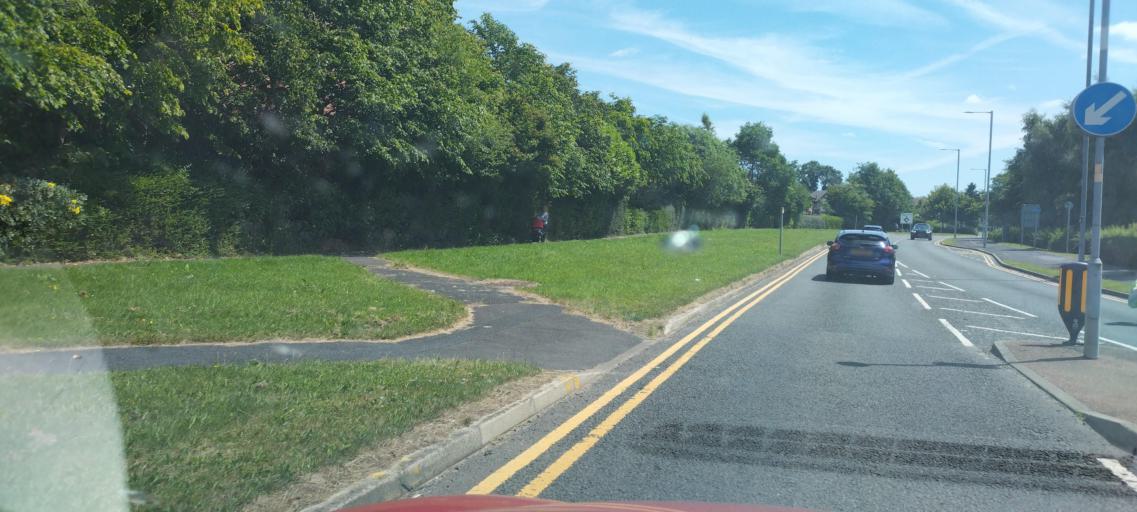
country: GB
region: England
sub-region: Borough of Bolton
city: Horwich
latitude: 53.5857
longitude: -2.5348
